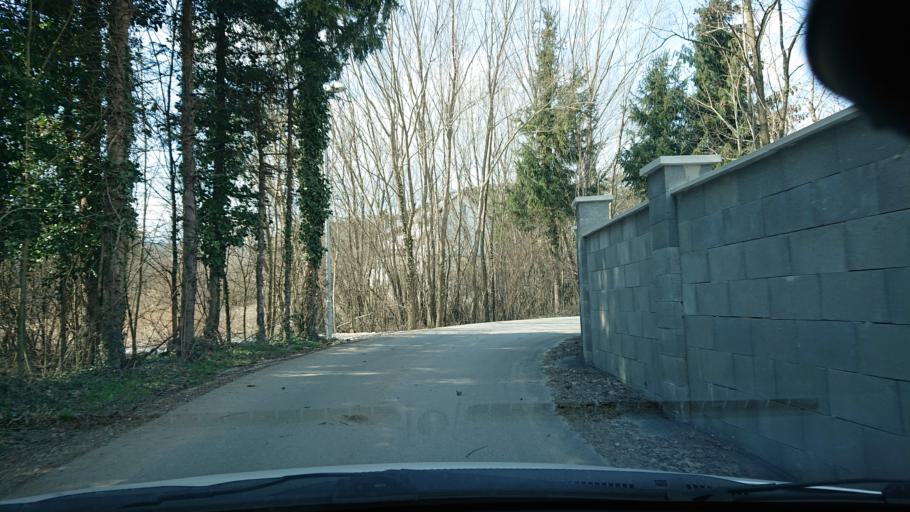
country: AT
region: Lower Austria
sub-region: Politischer Bezirk Baden
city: Pottenstein
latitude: 47.9370
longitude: 16.0789
